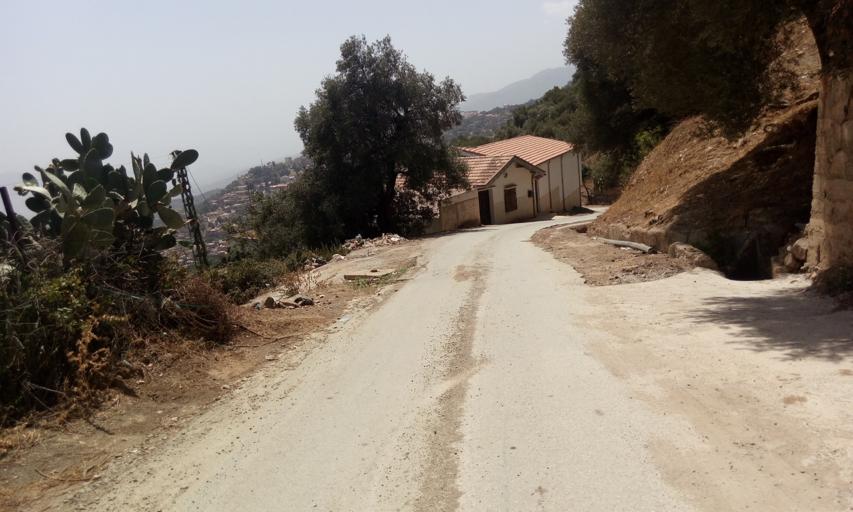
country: DZ
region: Tizi Ouzou
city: Chemini
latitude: 36.6075
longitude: 4.6320
